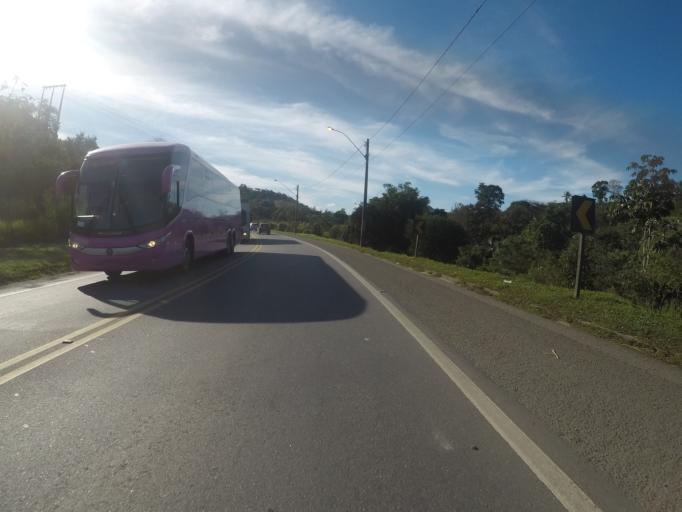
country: BR
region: Espirito Santo
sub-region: Fundao
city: Fundao
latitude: -19.9278
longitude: -40.4057
